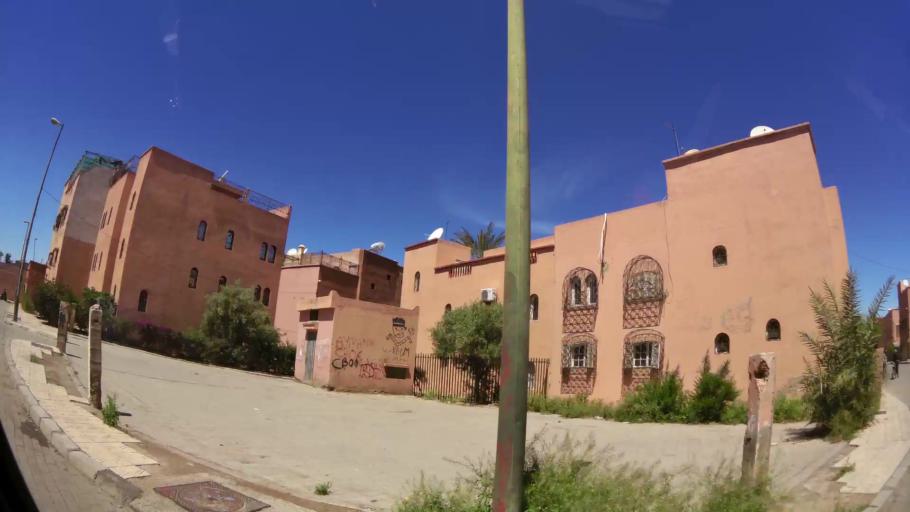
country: MA
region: Marrakech-Tensift-Al Haouz
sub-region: Marrakech
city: Marrakesh
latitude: 31.6502
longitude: -7.9940
